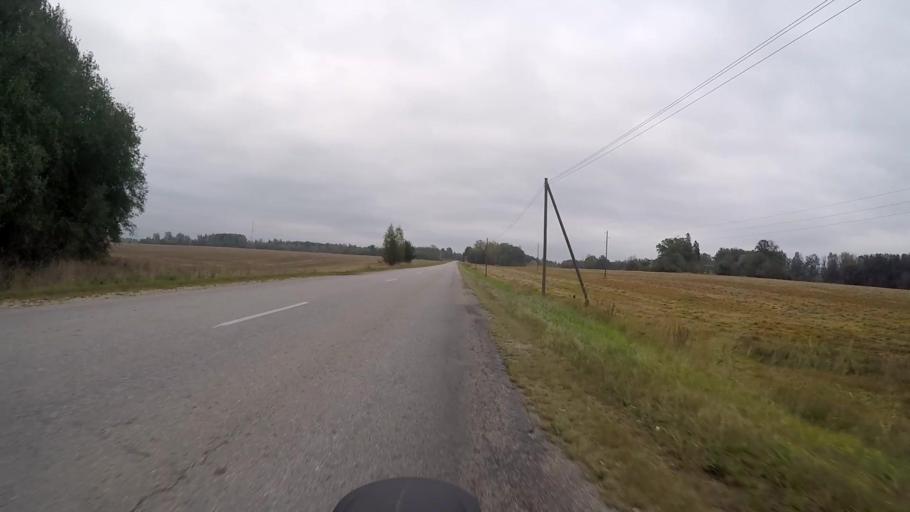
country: LV
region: Seja
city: Loja
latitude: 57.2747
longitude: 24.5686
